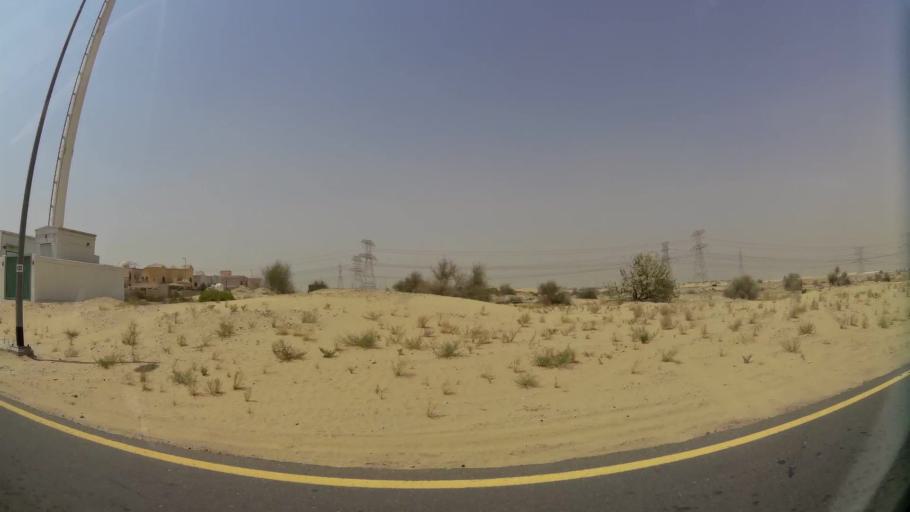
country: AE
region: Ash Shariqah
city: Sharjah
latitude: 25.2588
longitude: 55.4883
